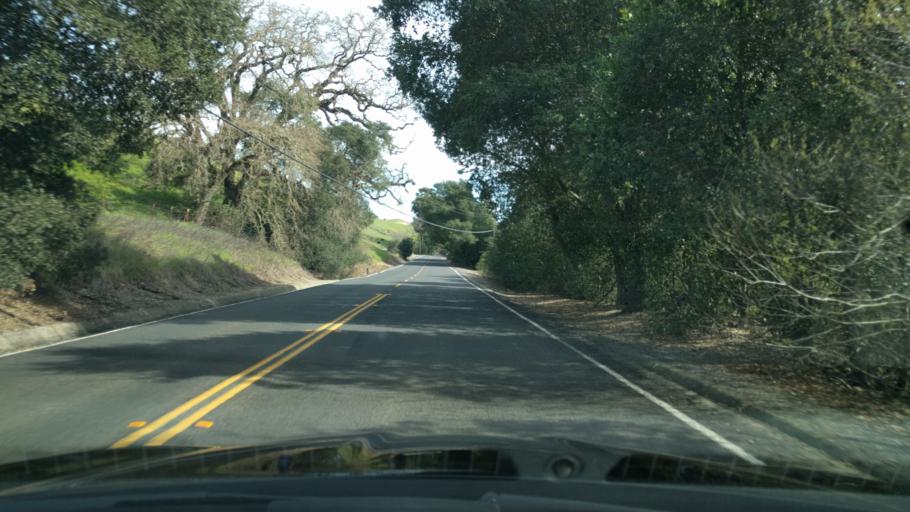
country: US
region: California
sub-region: Contra Costa County
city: Danville
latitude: 37.7929
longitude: -122.0154
